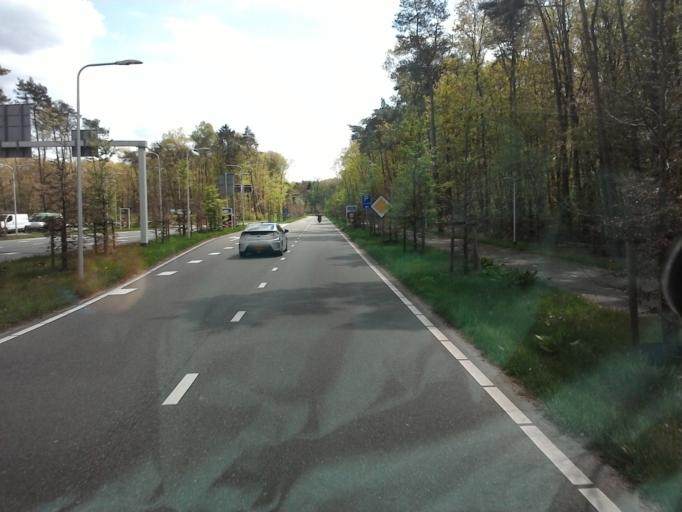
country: NL
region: Utrecht
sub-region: Gemeente Zeist
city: Zeist
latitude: 52.1044
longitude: 5.2630
